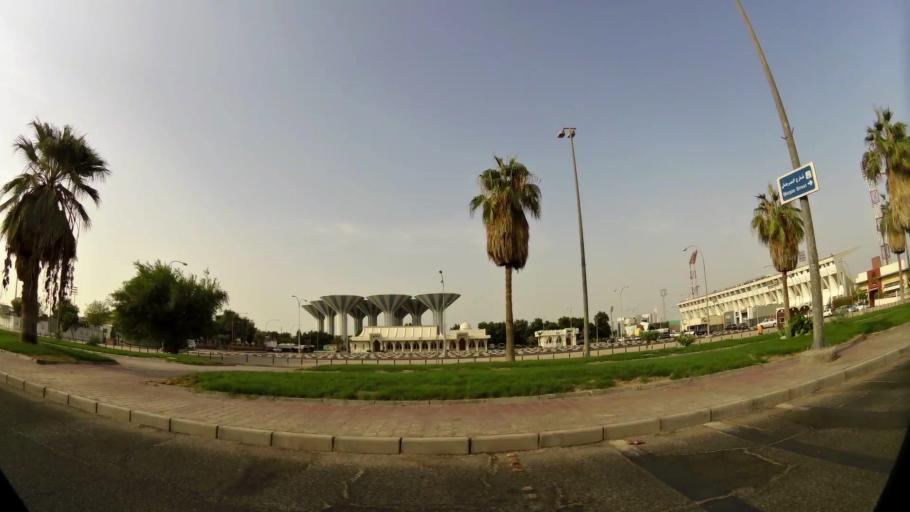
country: KW
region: Al Asimah
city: Ash Shamiyah
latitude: 29.3271
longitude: 47.9862
